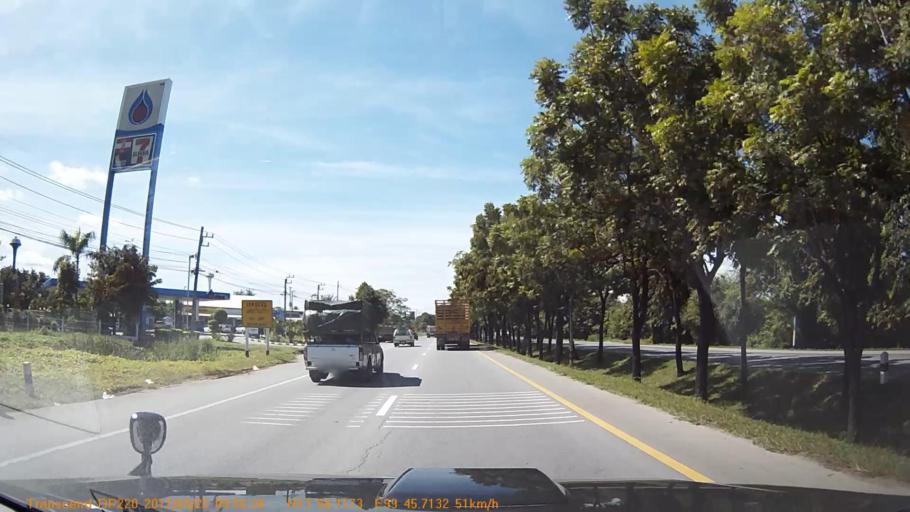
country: TH
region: Kanchanaburi
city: Tha Maka
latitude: 13.9348
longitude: 99.7619
